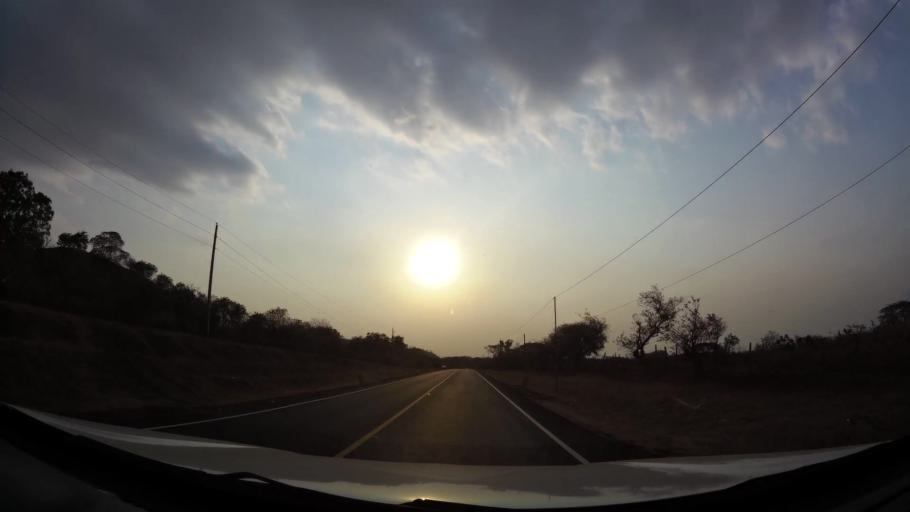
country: NI
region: Leon
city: Nagarote
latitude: 12.2784
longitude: -86.5048
